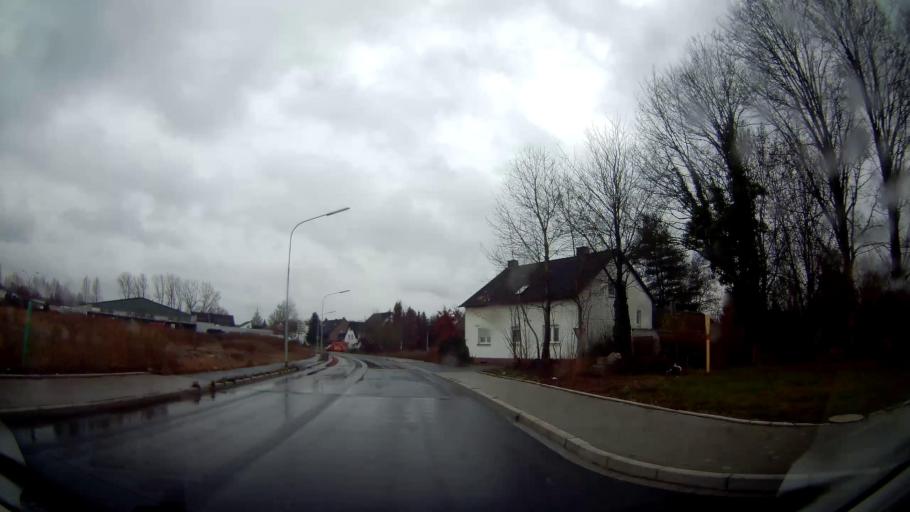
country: DE
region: North Rhine-Westphalia
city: Bochum-Hordel
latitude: 51.5216
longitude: 7.1978
